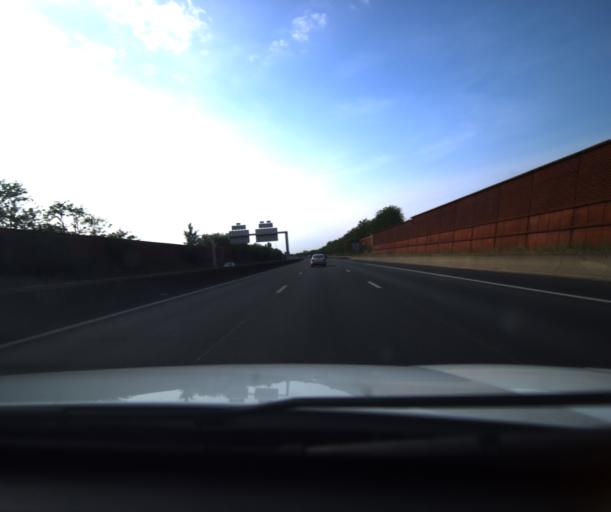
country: FR
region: Midi-Pyrenees
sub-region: Departement de la Haute-Garonne
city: Aucamville
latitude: 43.6640
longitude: 1.4231
